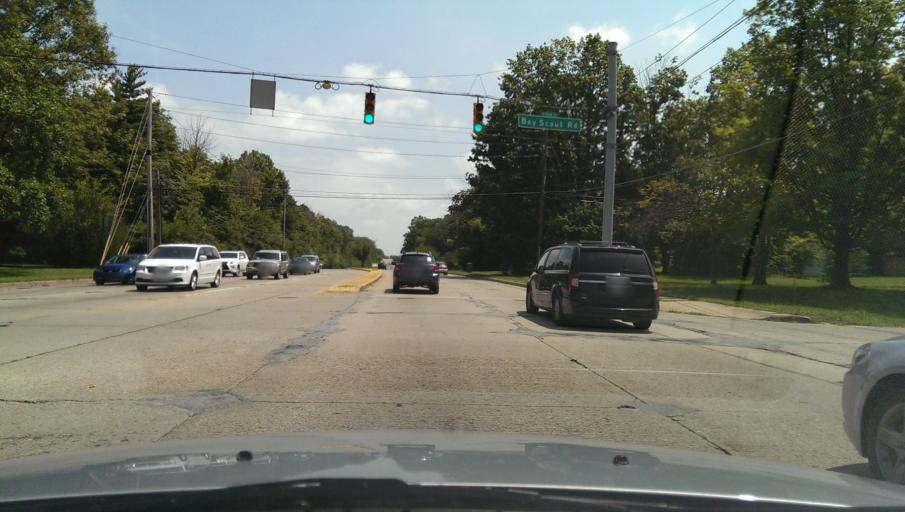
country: US
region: Indiana
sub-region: Marion County
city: Lawrence
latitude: 39.8549
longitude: -86.0327
